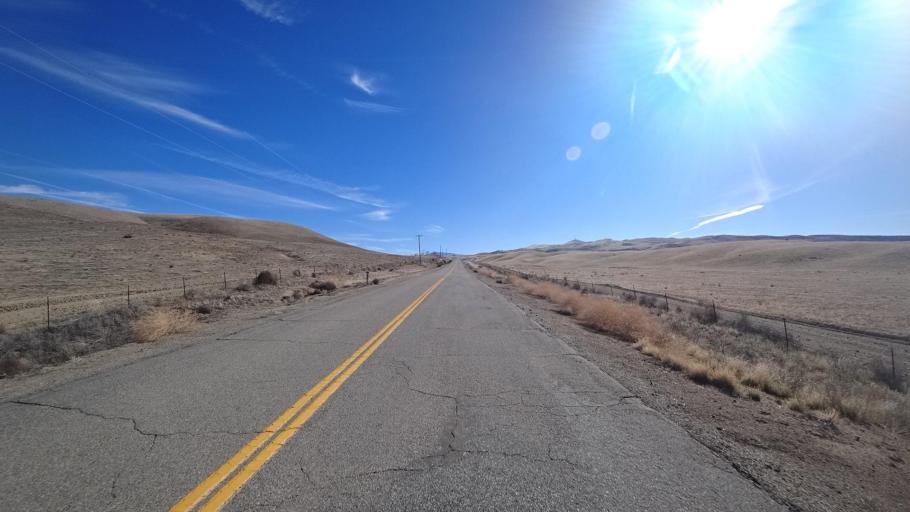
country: US
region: California
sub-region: Kern County
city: Maricopa
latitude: 34.9572
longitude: -119.4369
